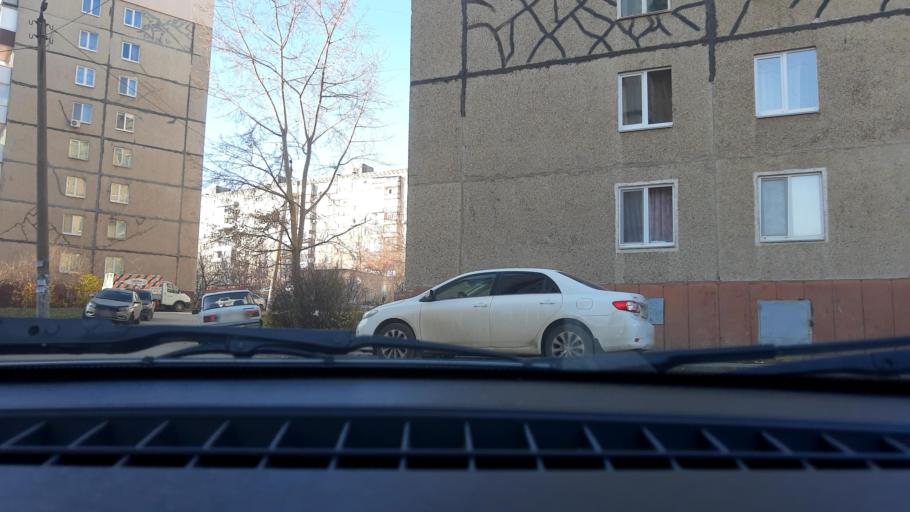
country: RU
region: Bashkortostan
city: Ufa
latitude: 54.7714
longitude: 56.0364
